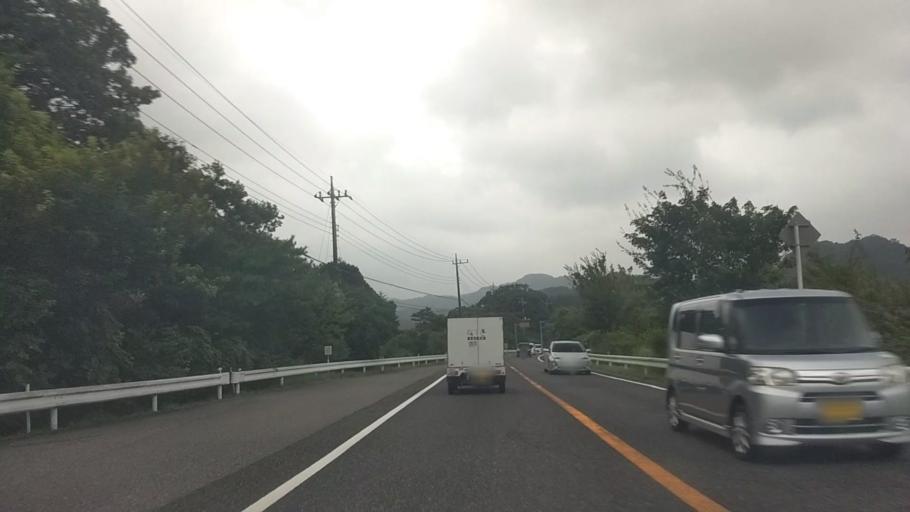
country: JP
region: Chiba
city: Kawaguchi
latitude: 35.1613
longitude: 140.0633
